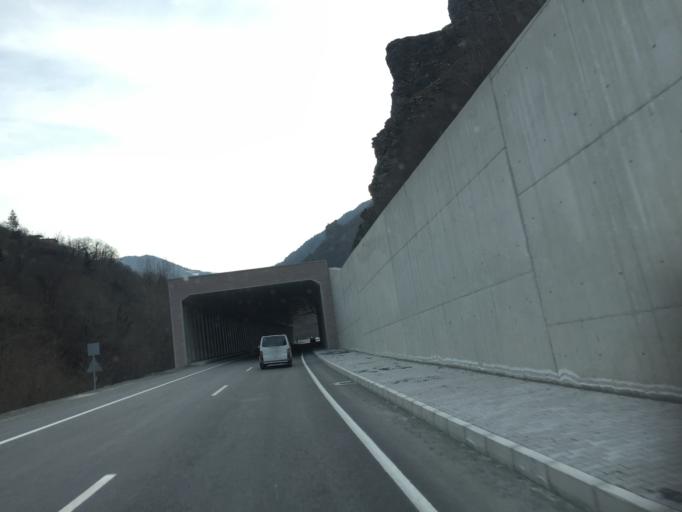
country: TR
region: Trabzon
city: Macka
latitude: 40.7748
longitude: 39.5675
